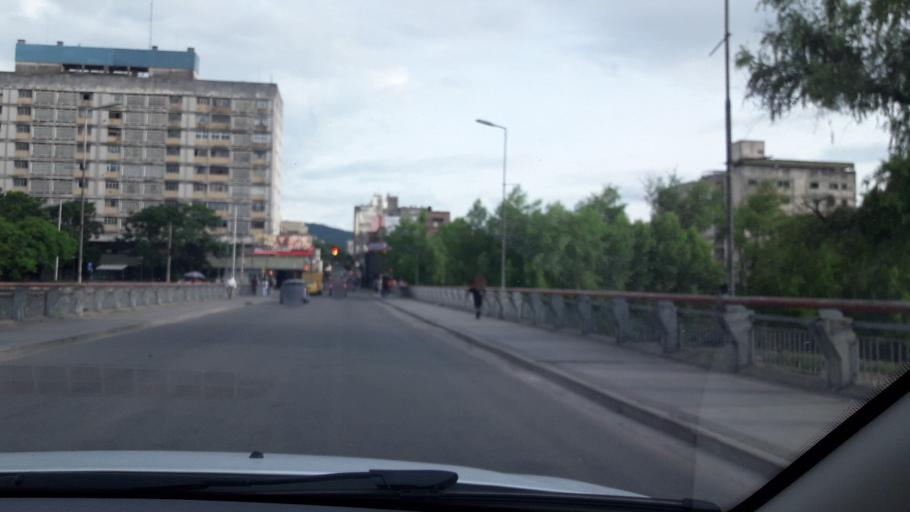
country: AR
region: Jujuy
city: San Salvador de Jujuy
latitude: -24.1898
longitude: -65.3025
